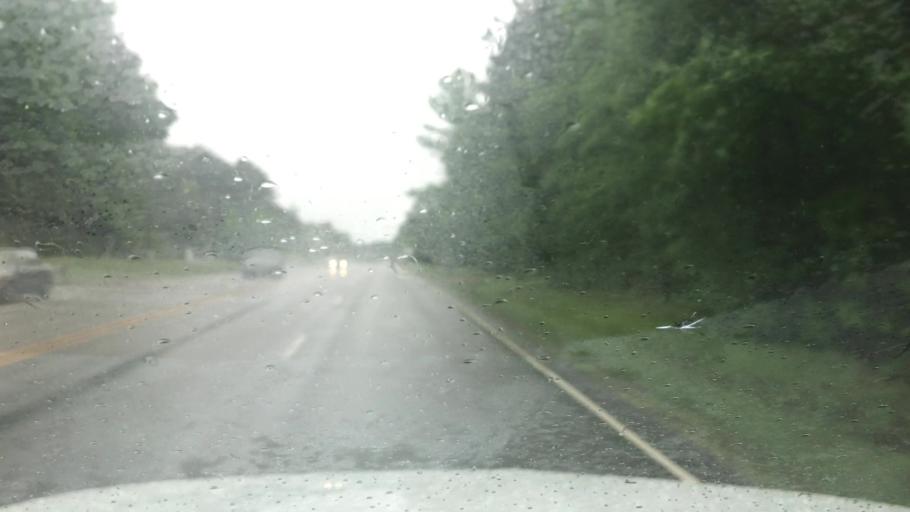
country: US
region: Virginia
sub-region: Hanover County
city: Ashland
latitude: 37.8137
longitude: -77.4737
